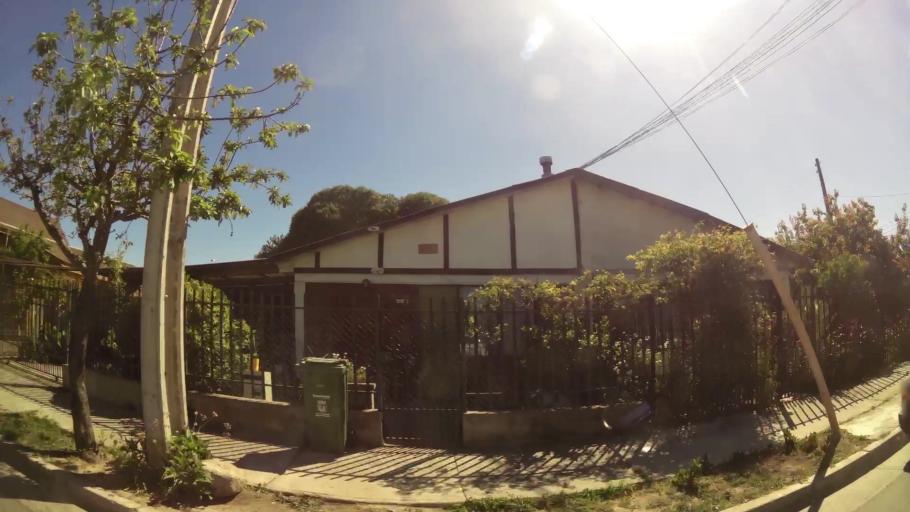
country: CL
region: Valparaiso
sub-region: Provincia de Marga Marga
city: Quilpue
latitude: -33.3144
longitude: -71.4068
